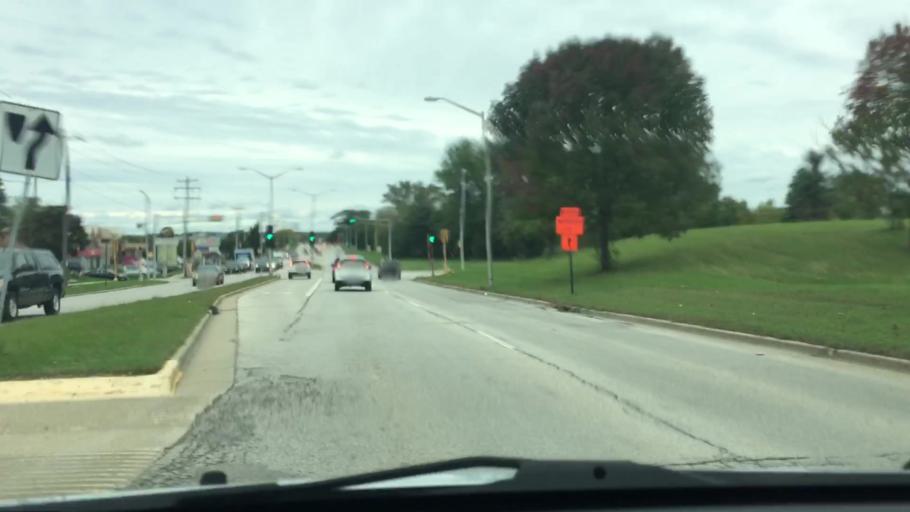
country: US
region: Wisconsin
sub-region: Waukesha County
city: Waukesha
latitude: 43.0362
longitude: -88.2558
